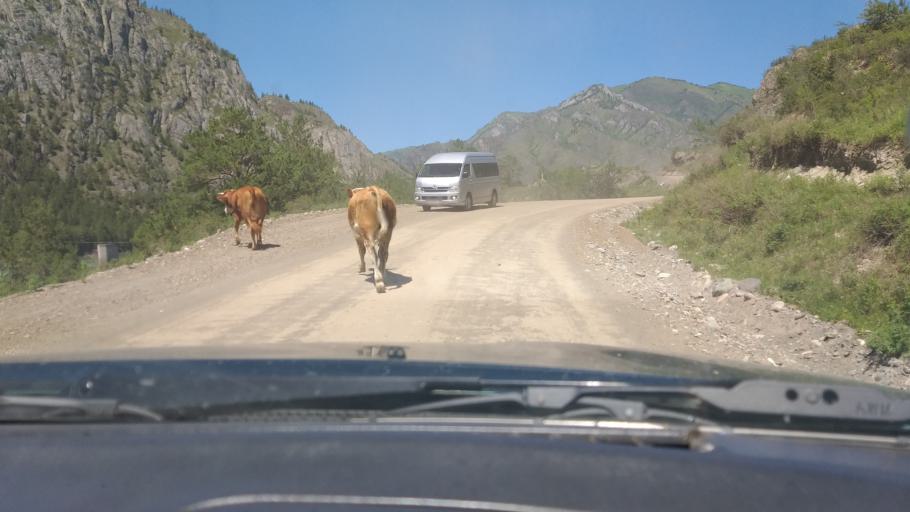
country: RU
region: Altay
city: Chemal
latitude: 51.2067
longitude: 86.0855
